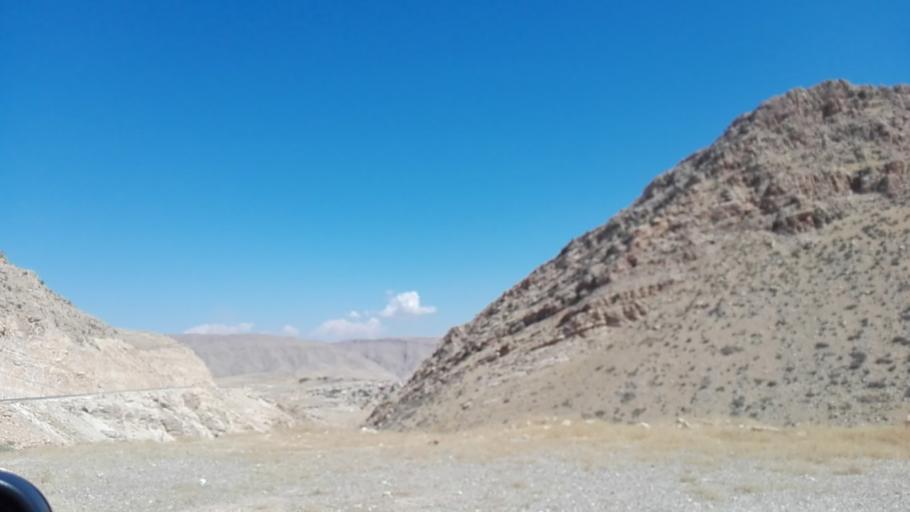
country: TR
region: Batman
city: Hasankeyf
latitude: 37.6968
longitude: 41.4585
